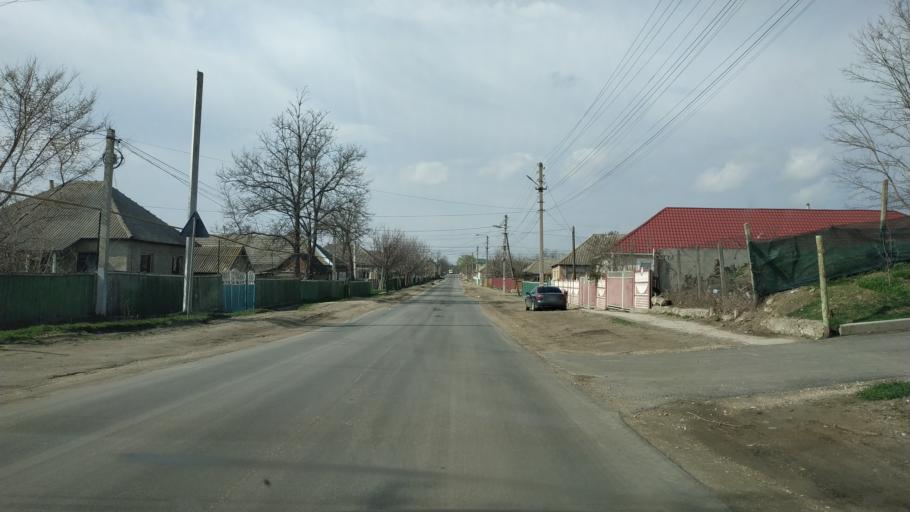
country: MD
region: Gagauzia
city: Vulcanesti
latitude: 45.6749
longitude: 28.4174
